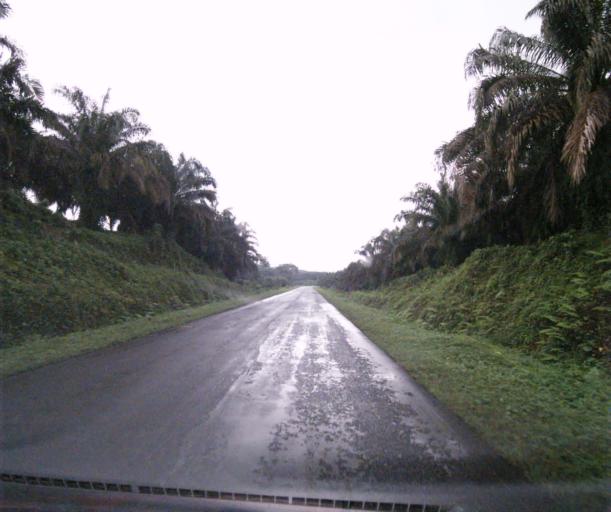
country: CM
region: South-West Province
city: Idenao
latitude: 4.1229
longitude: 8.9906
